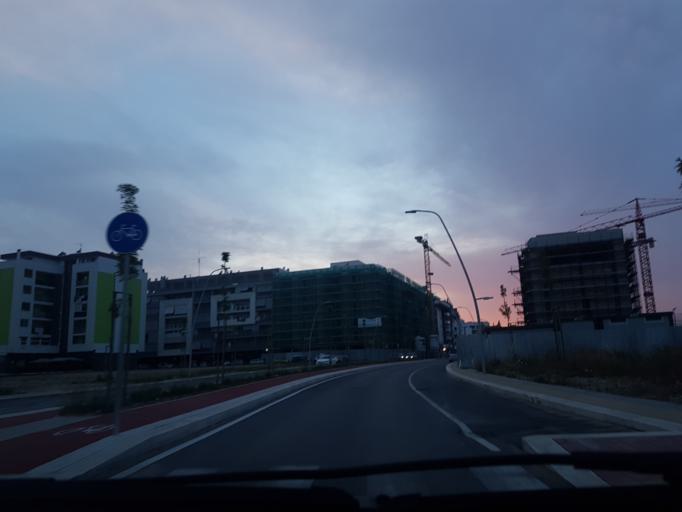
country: IT
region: Apulia
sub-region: Provincia di Barletta - Andria - Trani
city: Barletta
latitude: 41.3049
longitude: 16.2690
